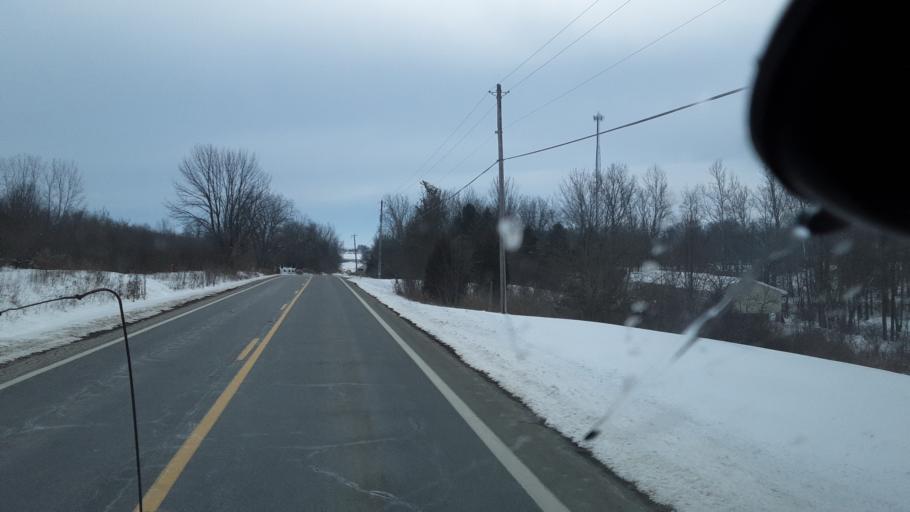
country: US
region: Ohio
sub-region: Madison County
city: Choctaw Lake
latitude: 39.9516
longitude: -83.5043
